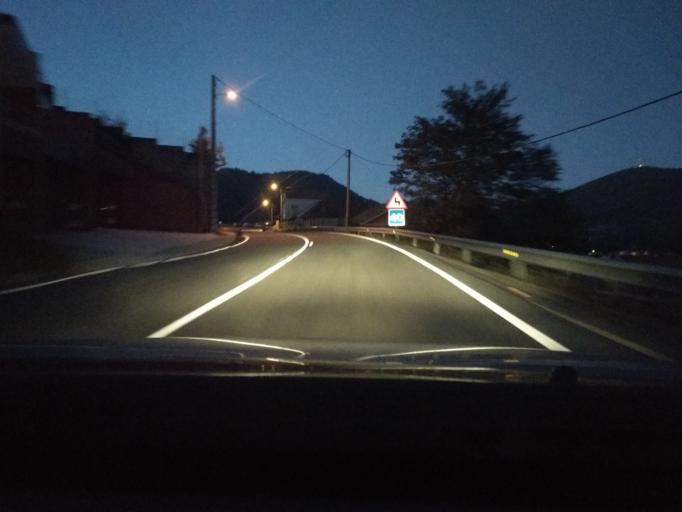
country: ES
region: Galicia
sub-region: Provincia de Pontevedra
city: Moana
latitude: 42.2965
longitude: -8.7418
